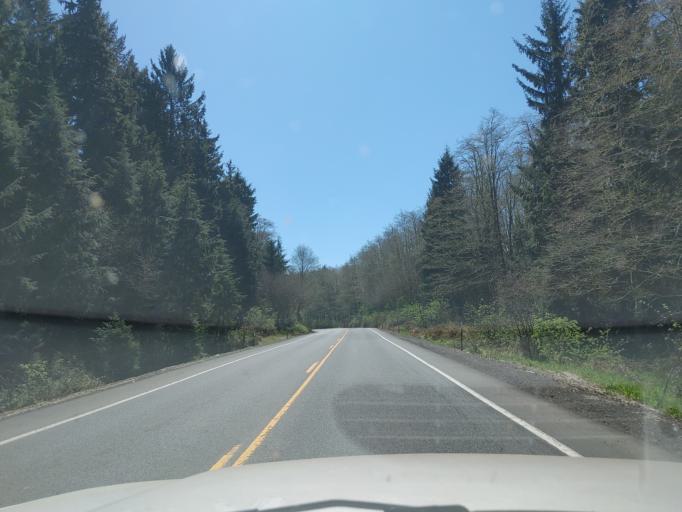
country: US
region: Oregon
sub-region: Clatsop County
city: Warrenton
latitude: 46.1483
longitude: -123.9020
